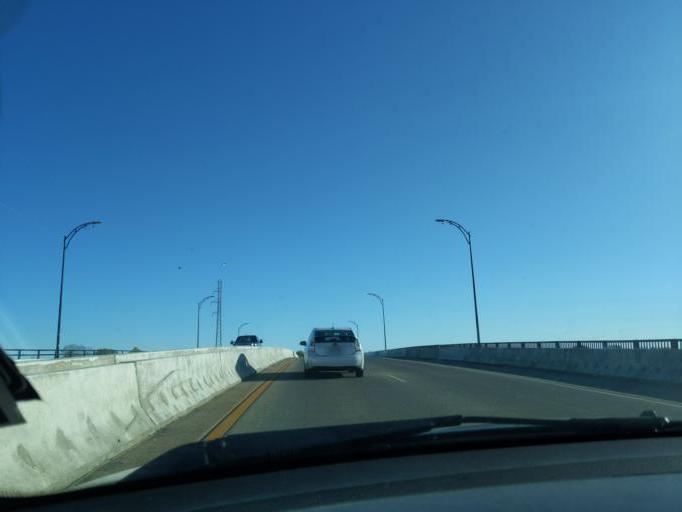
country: US
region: Massachusetts
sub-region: Essex County
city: Salem
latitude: 42.5381
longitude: -70.8878
